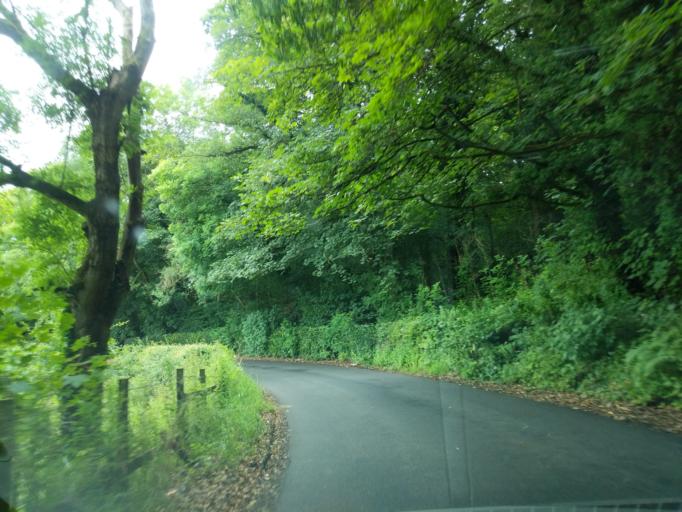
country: GB
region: Scotland
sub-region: South Lanarkshire
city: Dalserf
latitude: 55.7153
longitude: -3.8958
